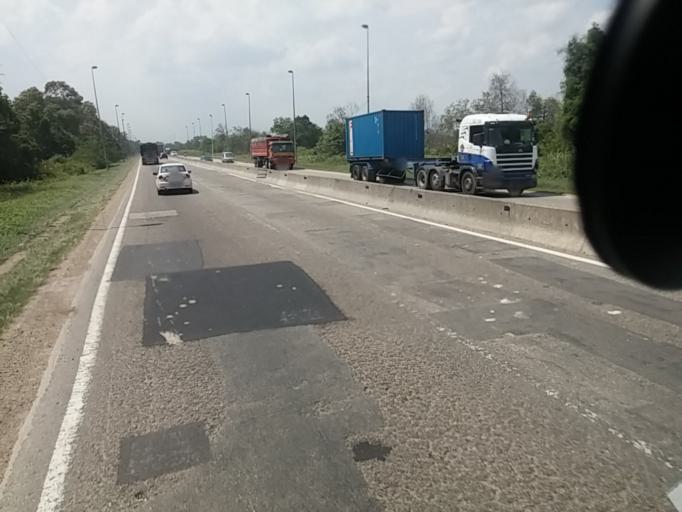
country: MY
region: Selangor
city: Klang
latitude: 2.9825
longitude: 101.3734
